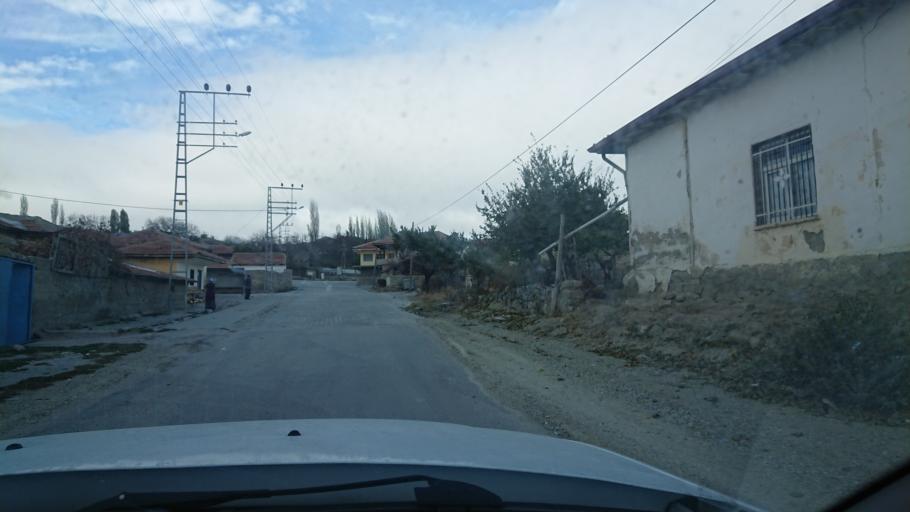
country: TR
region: Aksaray
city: Ortakoy
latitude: 38.7579
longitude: 34.0113
